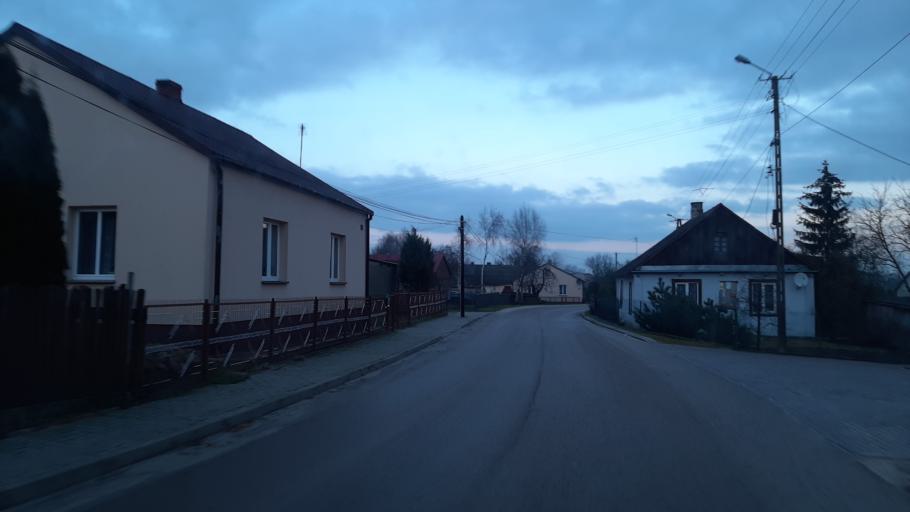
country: PL
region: Lublin Voivodeship
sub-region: Powiat lubartowski
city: Firlej
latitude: 51.5699
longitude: 22.5345
